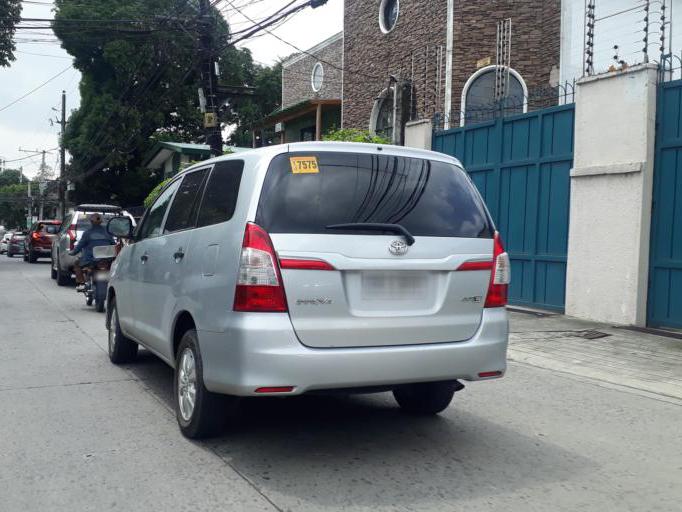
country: PH
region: Metro Manila
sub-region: San Juan
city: San Juan
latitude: 14.6164
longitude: 121.0469
